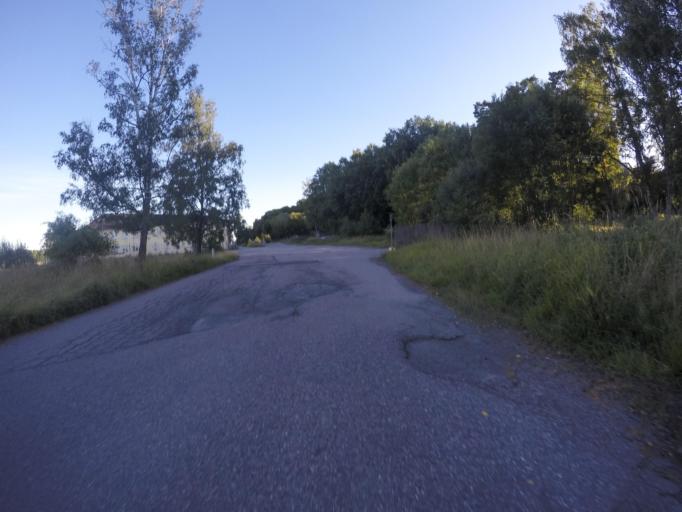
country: SE
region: Vaestmanland
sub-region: Vasteras
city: Vasteras
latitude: 59.5829
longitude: 16.6250
